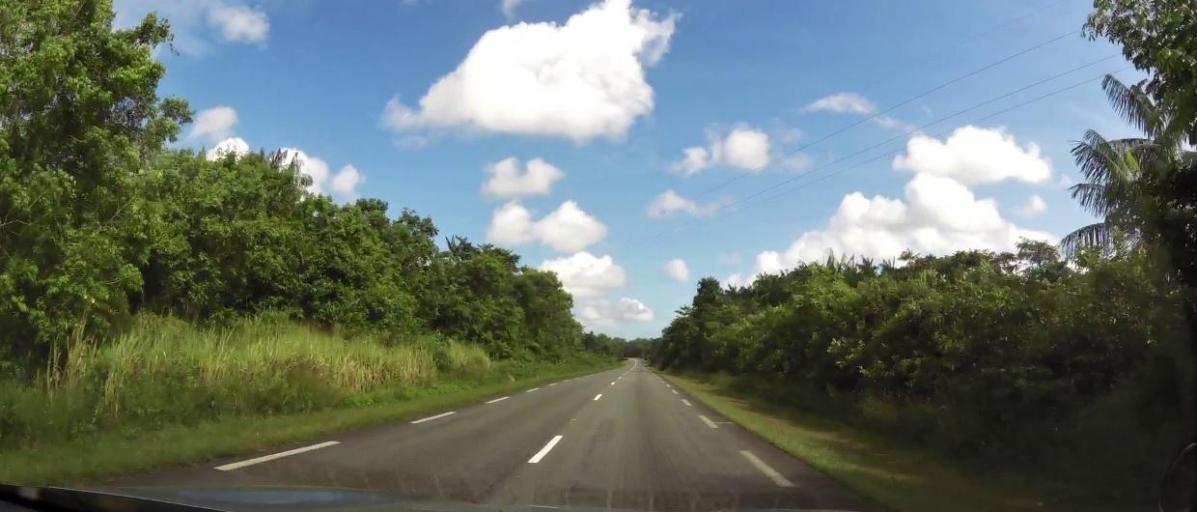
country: GF
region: Guyane
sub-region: Guyane
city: Sinnamary
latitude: 5.3699
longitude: -52.9641
